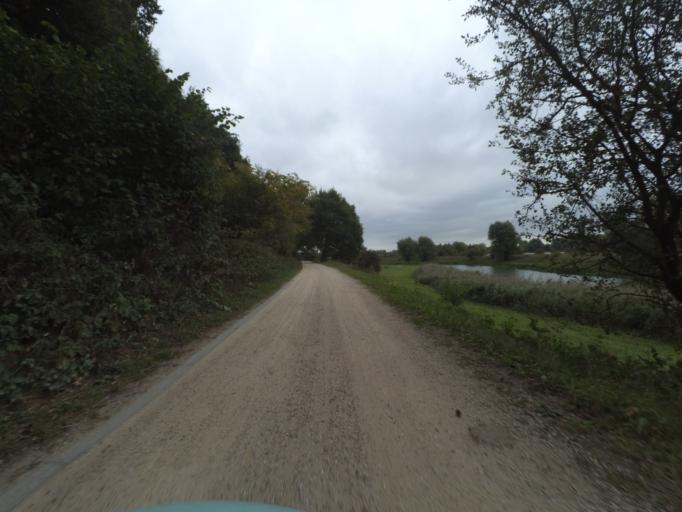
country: NL
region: Utrecht
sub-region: Gemeente Rhenen
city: Rhenen
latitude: 51.9518
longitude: 5.6049
